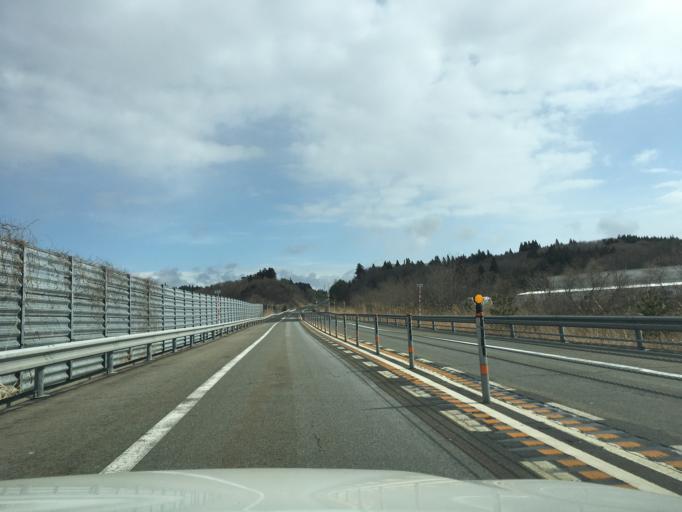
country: JP
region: Akita
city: Akita
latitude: 39.6262
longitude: 140.1587
